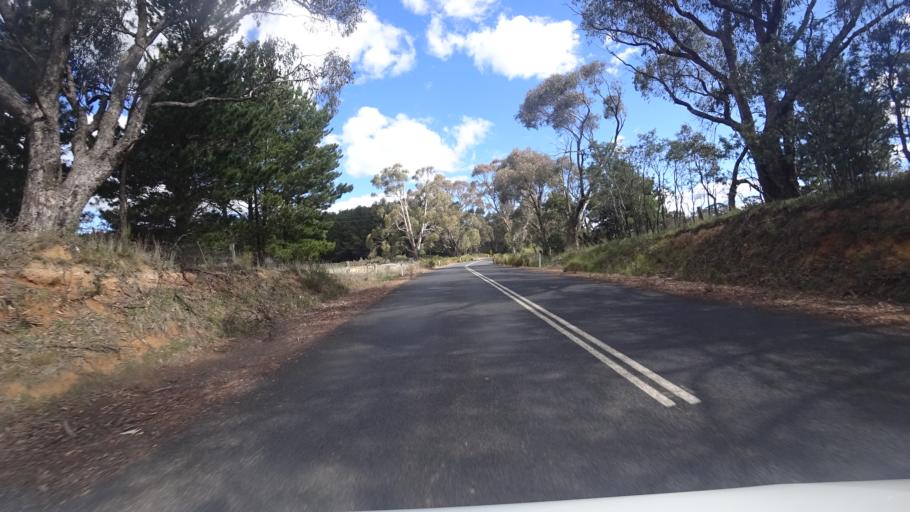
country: AU
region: New South Wales
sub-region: Oberon
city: Oberon
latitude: -33.6831
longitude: 149.7861
